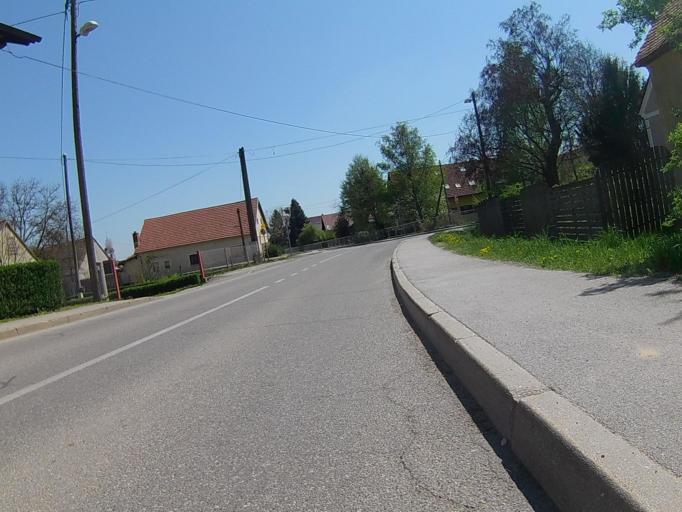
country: SI
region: Hoce-Slivnica
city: Spodnje Hoce
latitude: 46.5014
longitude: 15.6440
